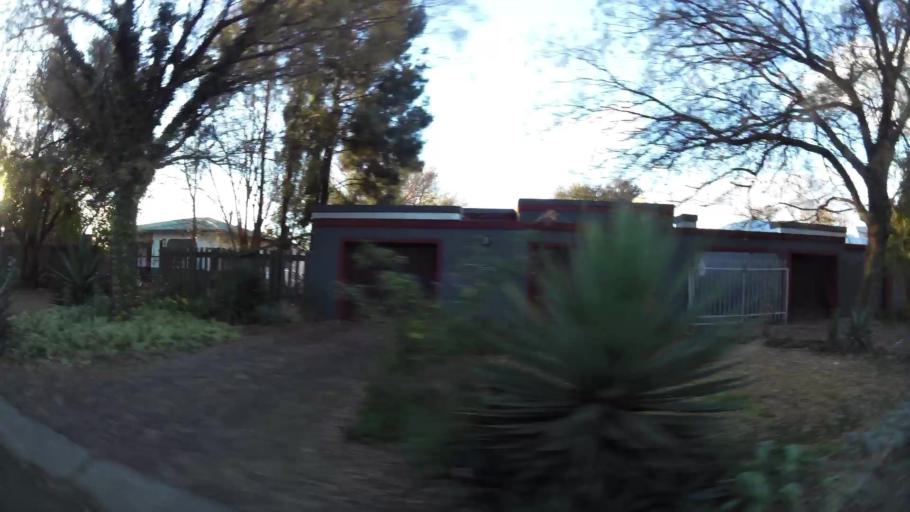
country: ZA
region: North-West
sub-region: Dr Kenneth Kaunda District Municipality
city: Potchefstroom
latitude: -26.7340
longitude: 27.0868
